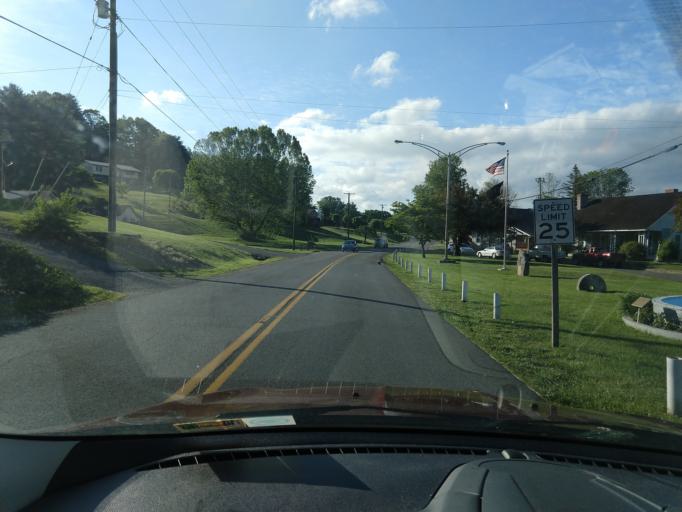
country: US
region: Virginia
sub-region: City of Galax
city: Galax
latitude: 36.7137
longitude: -80.9714
